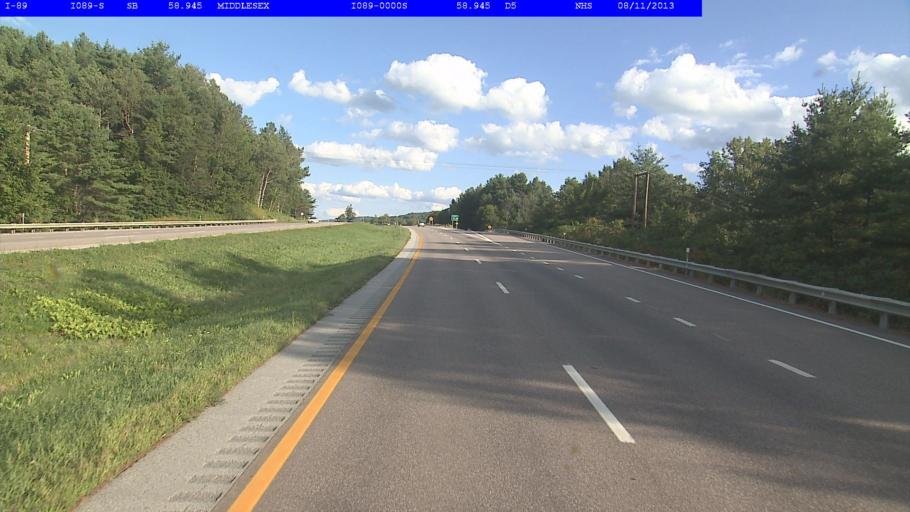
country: US
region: Vermont
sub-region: Washington County
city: Waterbury
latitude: 44.3008
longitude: -72.6882
